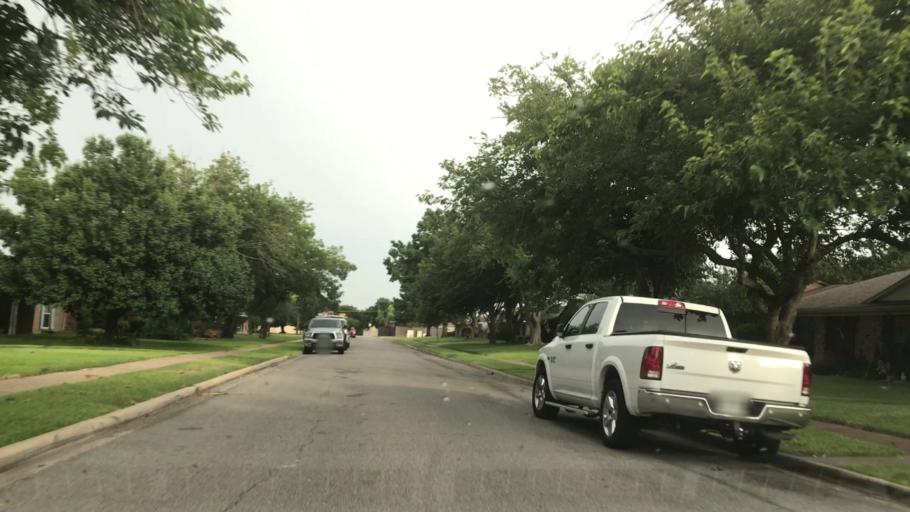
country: US
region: Texas
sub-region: Dallas County
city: Mesquite
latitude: 32.8338
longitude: -96.6371
